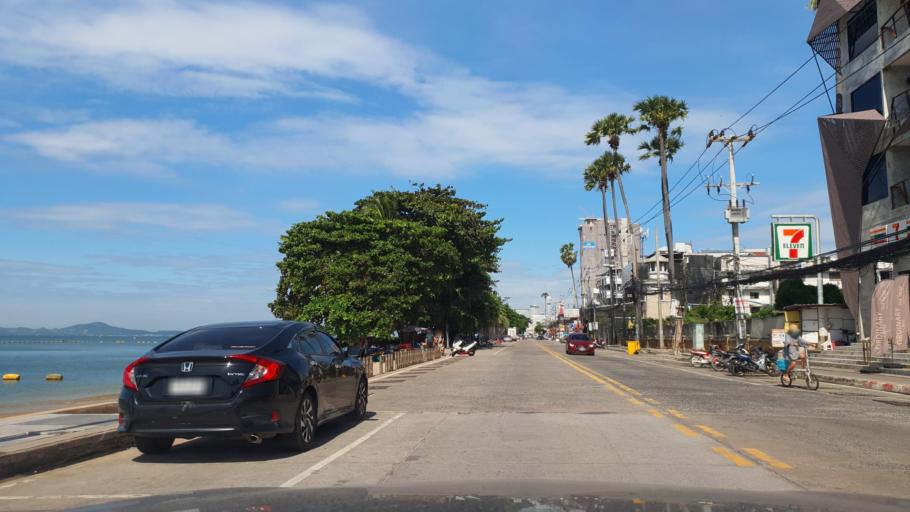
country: TH
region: Chon Buri
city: Phatthaya
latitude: 12.8828
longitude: 100.8807
